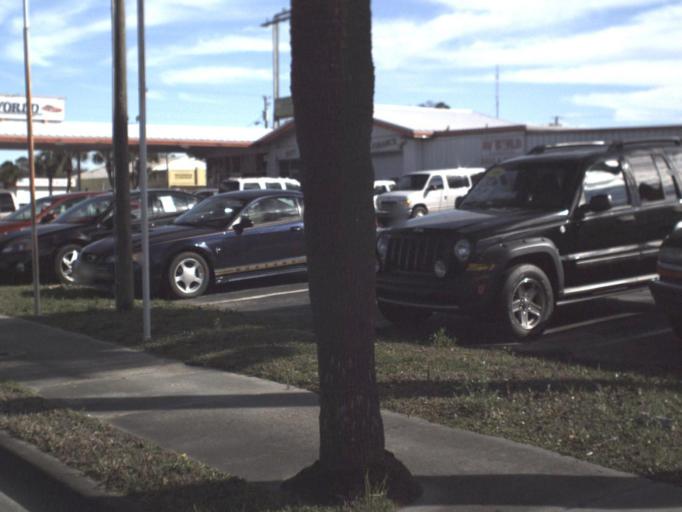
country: US
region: Florida
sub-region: Bay County
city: Panama City
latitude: 30.1743
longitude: -85.6601
